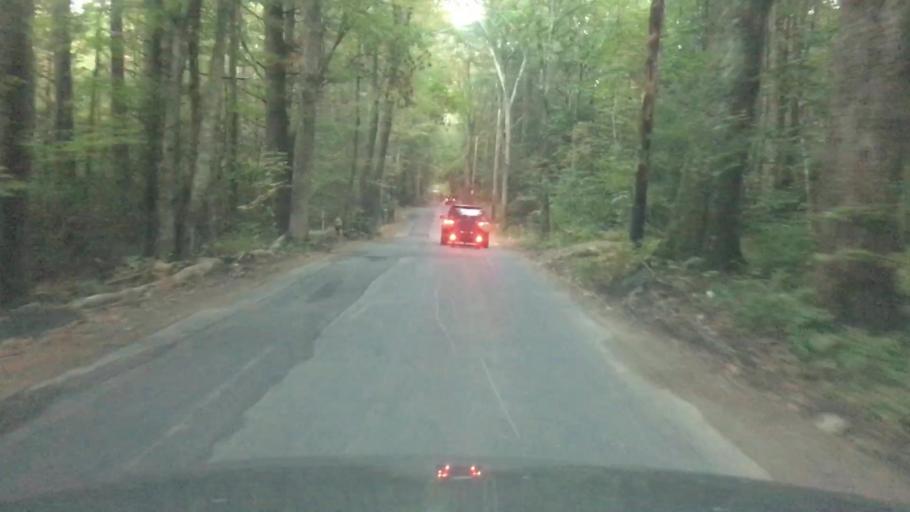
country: US
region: Massachusetts
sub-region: Worcester County
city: Southbridge
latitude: 42.1190
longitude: -72.0271
